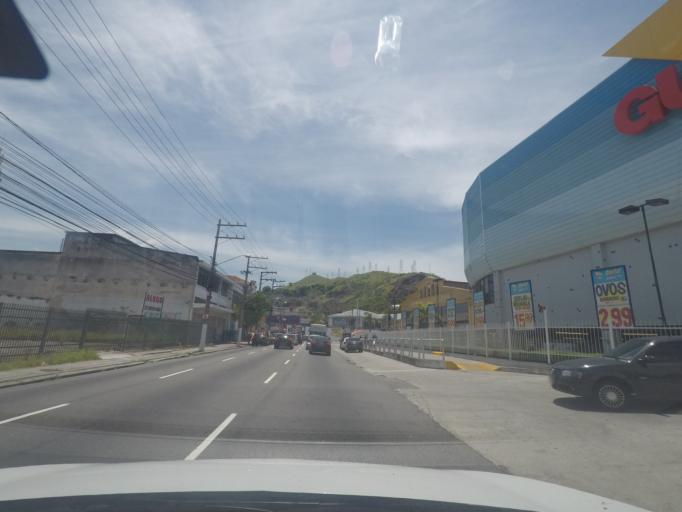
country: BR
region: Rio de Janeiro
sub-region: Niteroi
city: Niteroi
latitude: -22.8892
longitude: -43.1154
